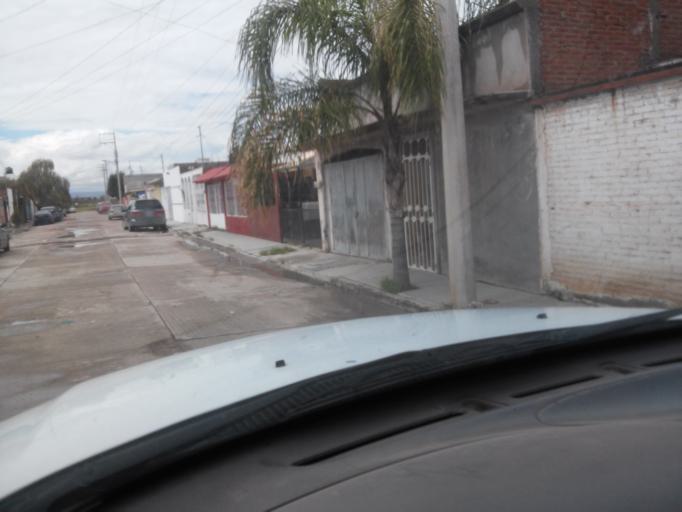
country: MX
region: Durango
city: Victoria de Durango
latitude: 24.0237
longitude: -104.6155
